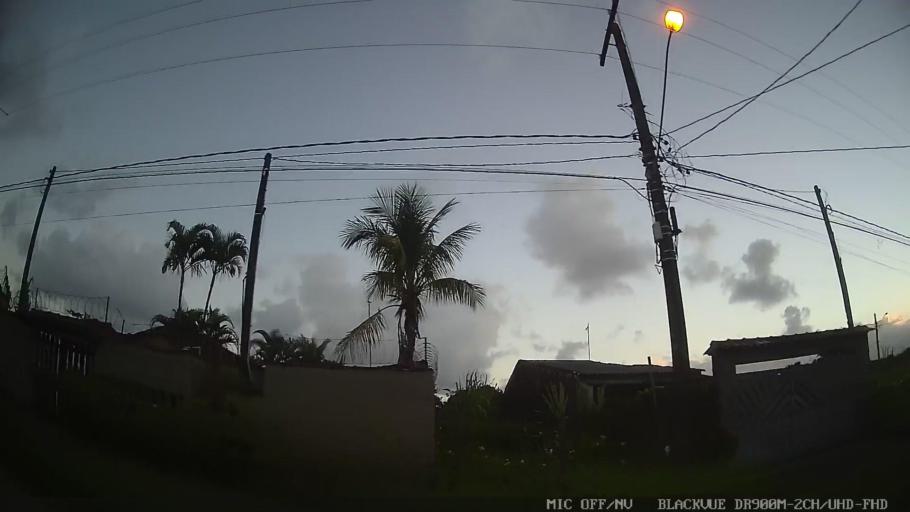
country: BR
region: Sao Paulo
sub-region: Itanhaem
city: Itanhaem
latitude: -24.1458
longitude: -46.7412
